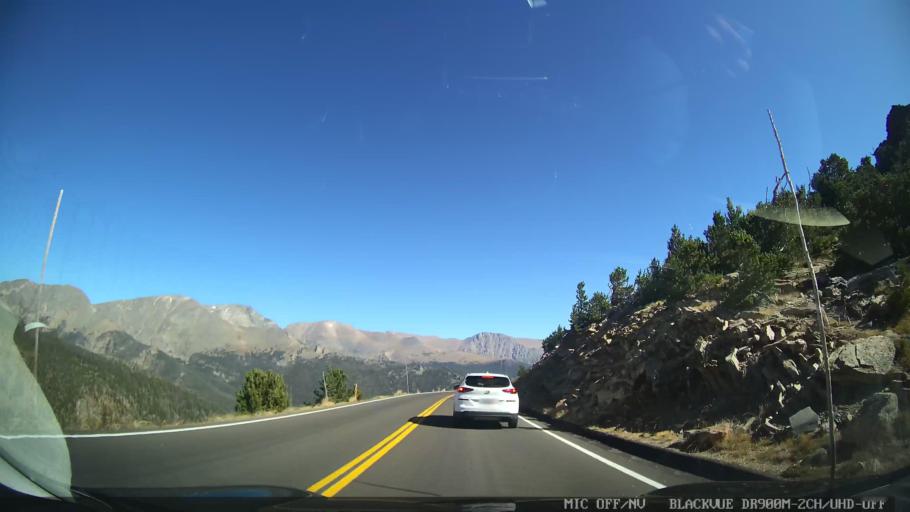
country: US
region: Colorado
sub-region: Larimer County
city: Estes Park
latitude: 40.3988
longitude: -105.6719
